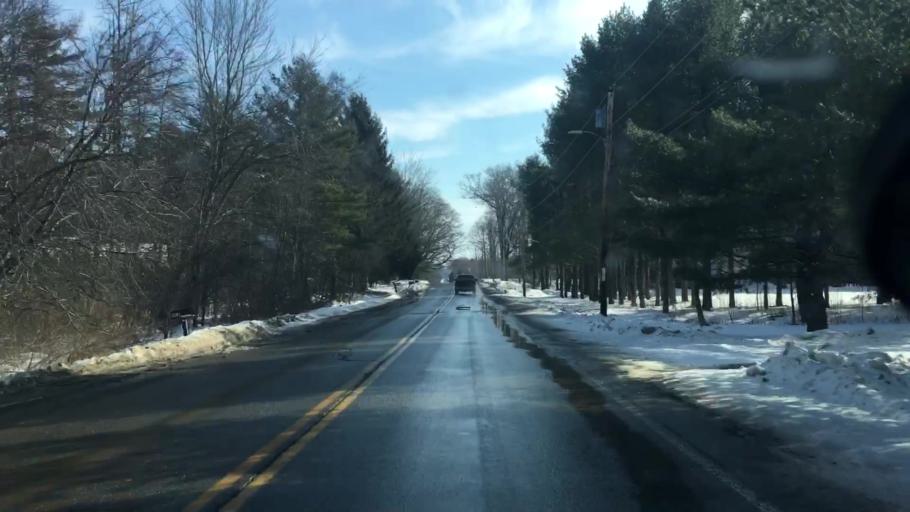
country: US
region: Maine
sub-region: Penobscot County
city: Bangor
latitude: 44.8469
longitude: -68.8380
